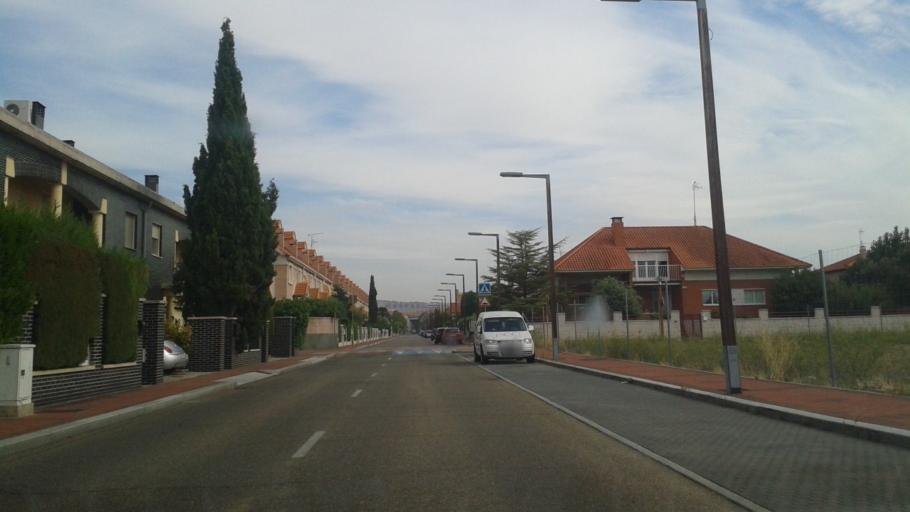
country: ES
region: Castille and Leon
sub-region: Provincia de Valladolid
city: Arroyo
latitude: 41.6135
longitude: -4.7824
